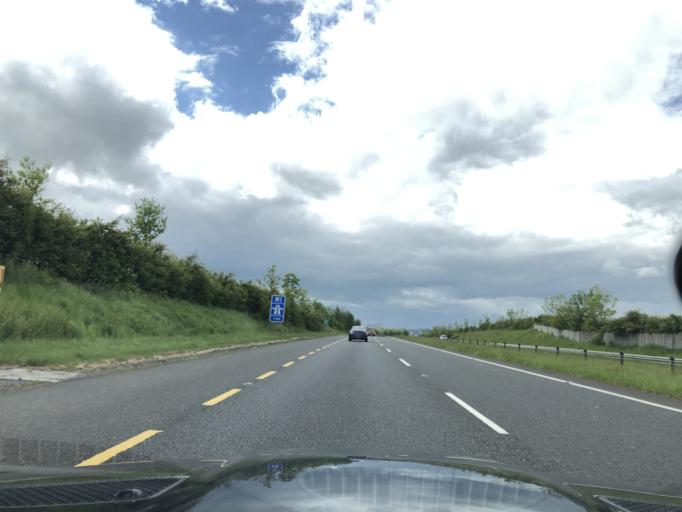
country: IE
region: Leinster
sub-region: Lu
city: Dundalk
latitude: 54.0433
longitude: -6.3683
